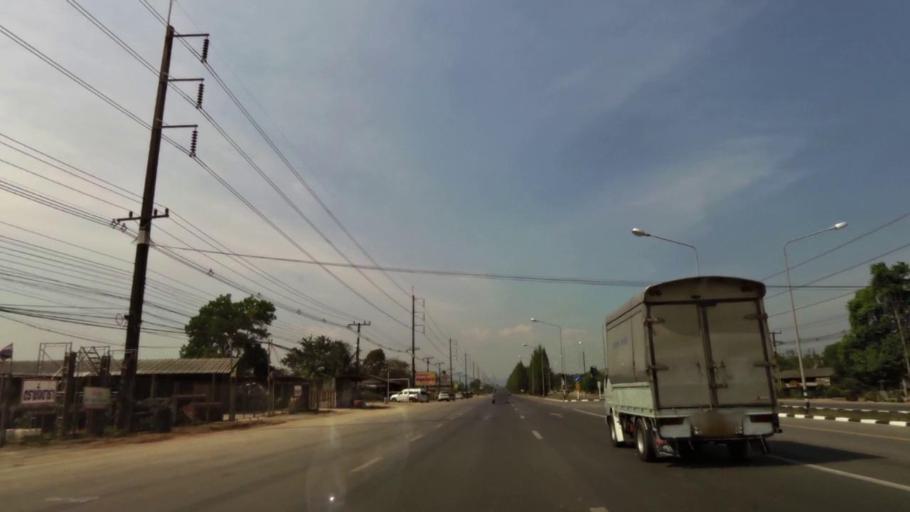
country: TH
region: Chanthaburi
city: Chanthaburi
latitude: 12.6290
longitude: 102.1461
